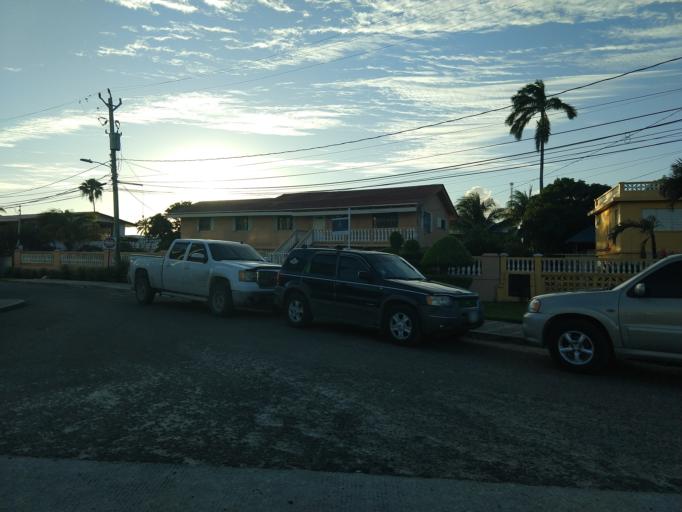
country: BZ
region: Belize
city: Belize City
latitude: 17.5102
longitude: -88.1875
